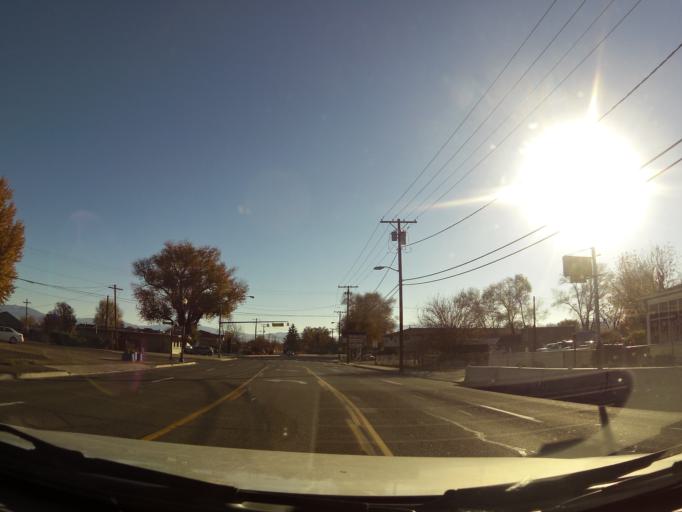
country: US
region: Nevada
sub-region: Douglas County
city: Gardnerville
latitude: 38.9395
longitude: -119.7467
